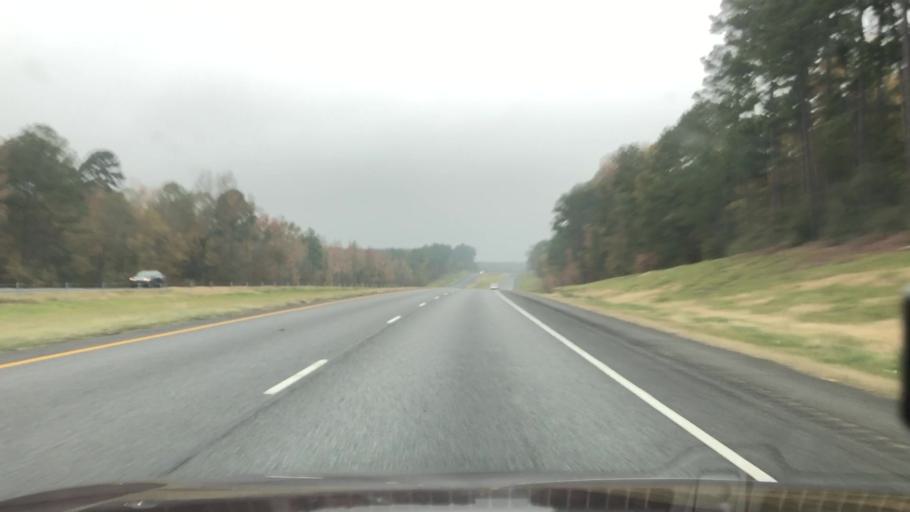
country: US
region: Louisiana
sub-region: Lincoln Parish
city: Ruston
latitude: 32.5224
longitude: -92.4179
